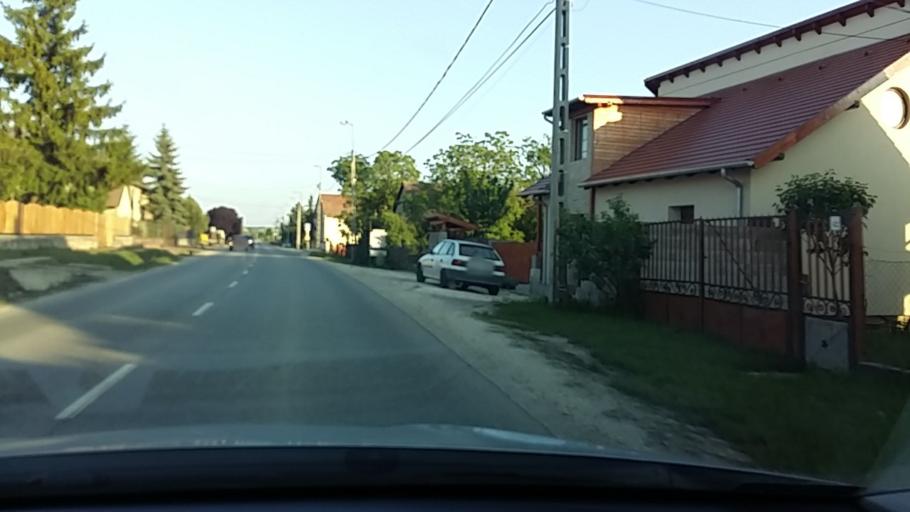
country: HU
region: Pest
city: Orbottyan
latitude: 47.6783
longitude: 19.2664
